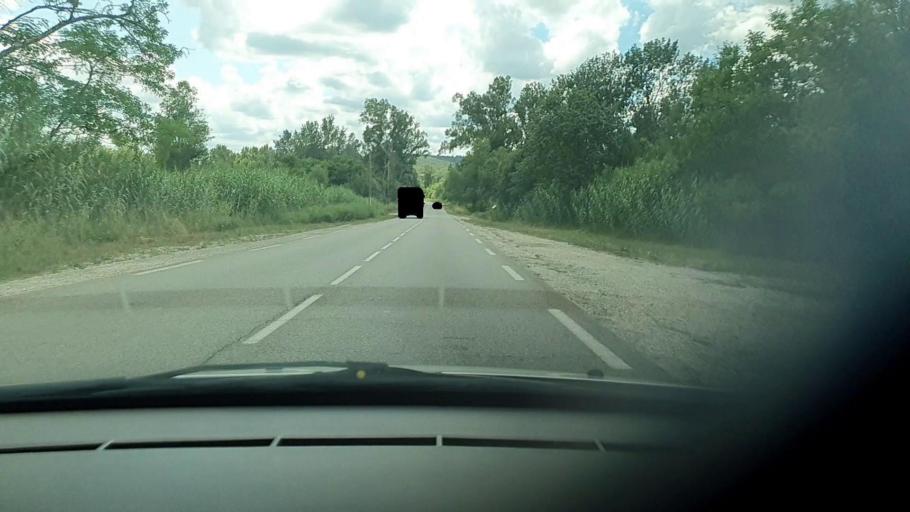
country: FR
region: Languedoc-Roussillon
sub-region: Departement du Gard
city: Moussac
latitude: 43.9827
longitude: 4.2123
